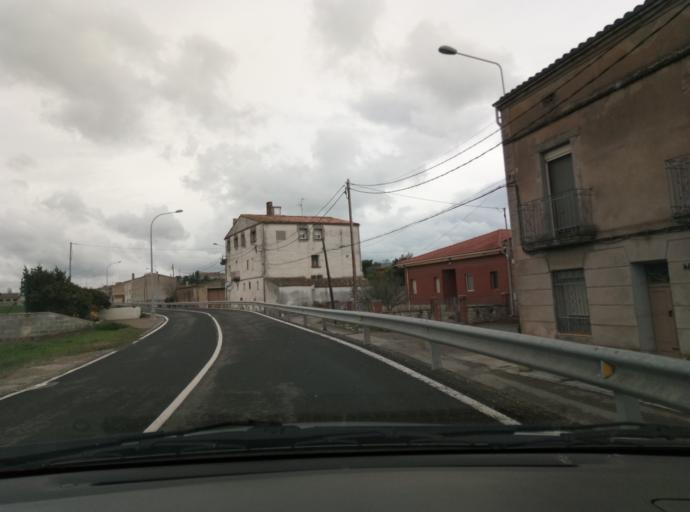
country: ES
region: Catalonia
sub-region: Provincia de Lleida
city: Cervera
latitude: 41.6318
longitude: 1.3384
